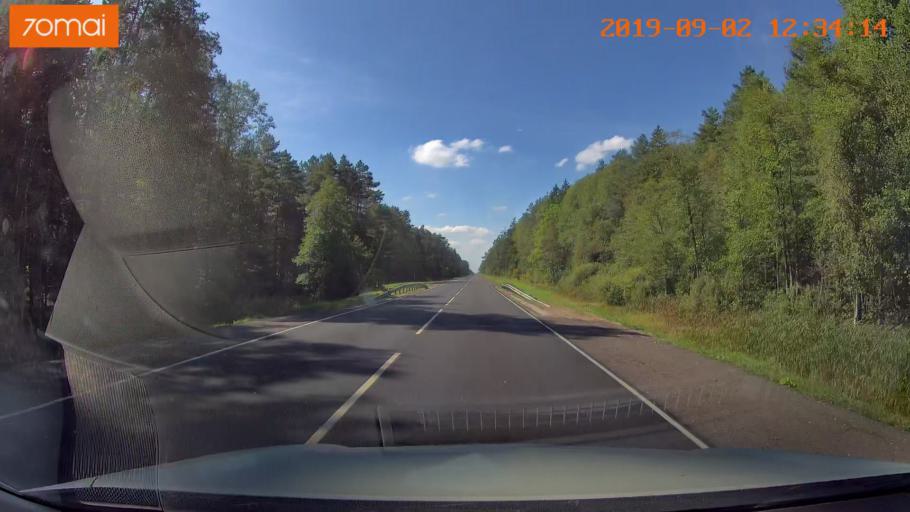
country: RU
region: Smolensk
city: Shumyachi
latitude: 53.8118
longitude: 32.4093
